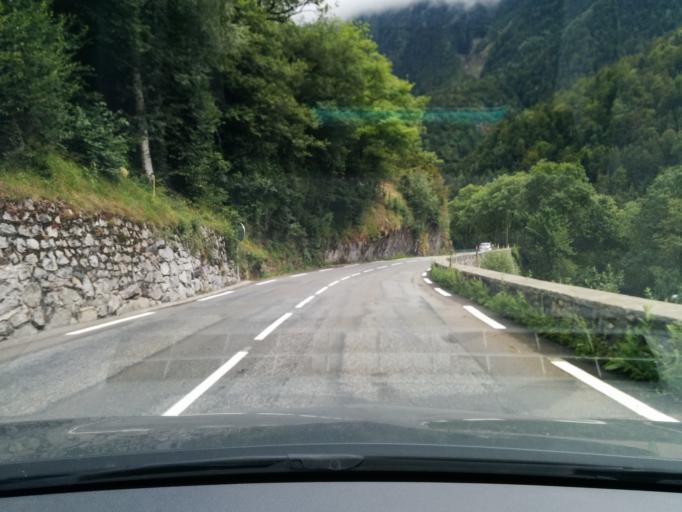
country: FR
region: Midi-Pyrenees
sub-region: Departement des Hautes-Pyrenees
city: Saint-Lary-Soulan
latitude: 42.7879
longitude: 0.2398
